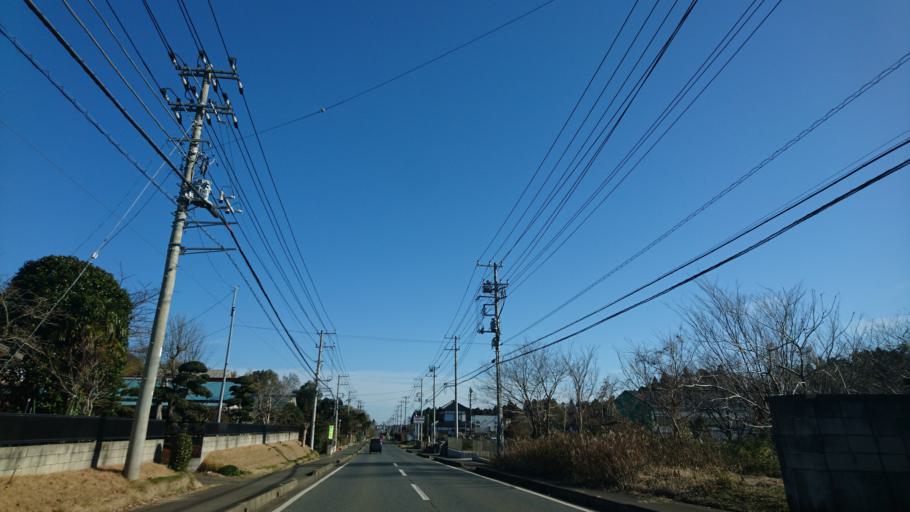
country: JP
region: Chiba
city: Oami
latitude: 35.5805
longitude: 140.3061
